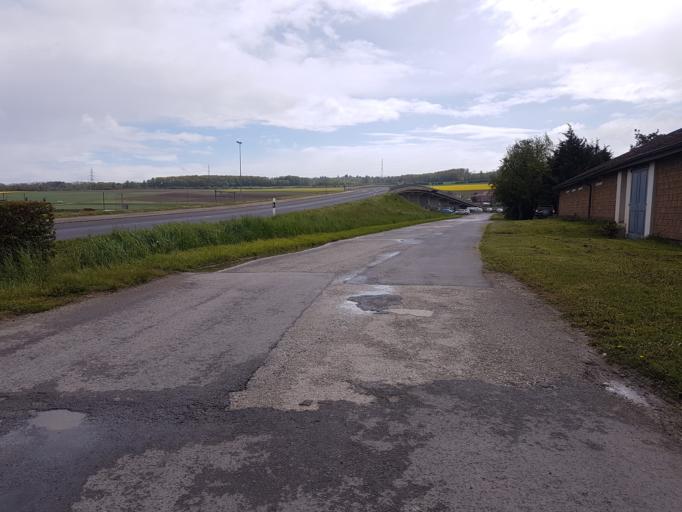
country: CH
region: Vaud
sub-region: Jura-Nord vaudois District
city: Bavois
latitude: 46.6878
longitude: 6.5568
